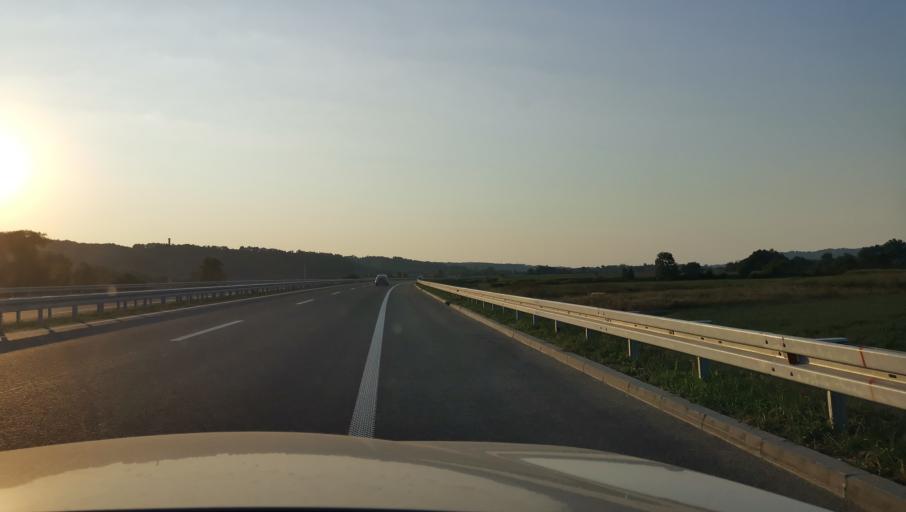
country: RS
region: Central Serbia
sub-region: Kolubarski Okrug
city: Ljig
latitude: 44.3099
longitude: 20.2224
